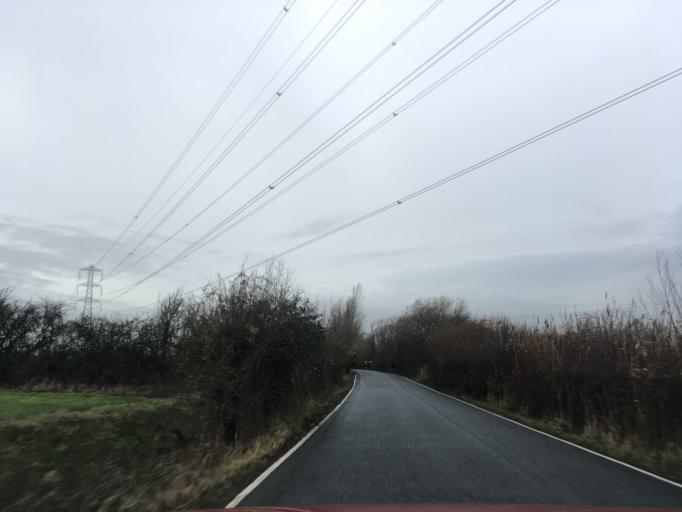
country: GB
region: Wales
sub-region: Newport
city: Bishton
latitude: 51.5600
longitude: -2.8933
